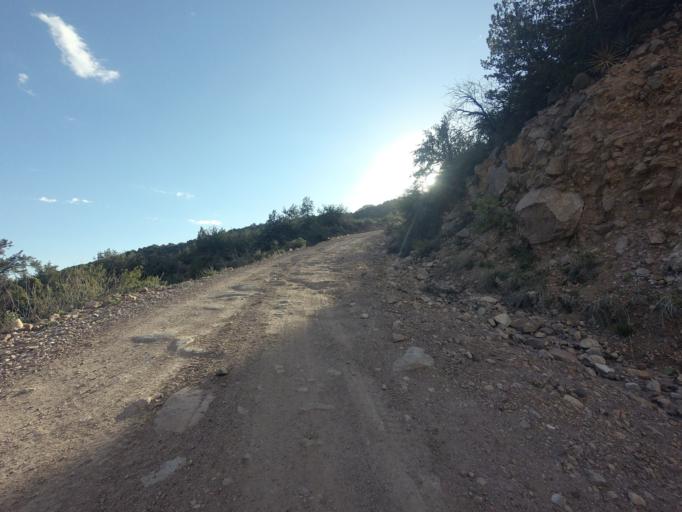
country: US
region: Arizona
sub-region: Gila County
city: Pine
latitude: 34.3769
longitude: -111.6604
